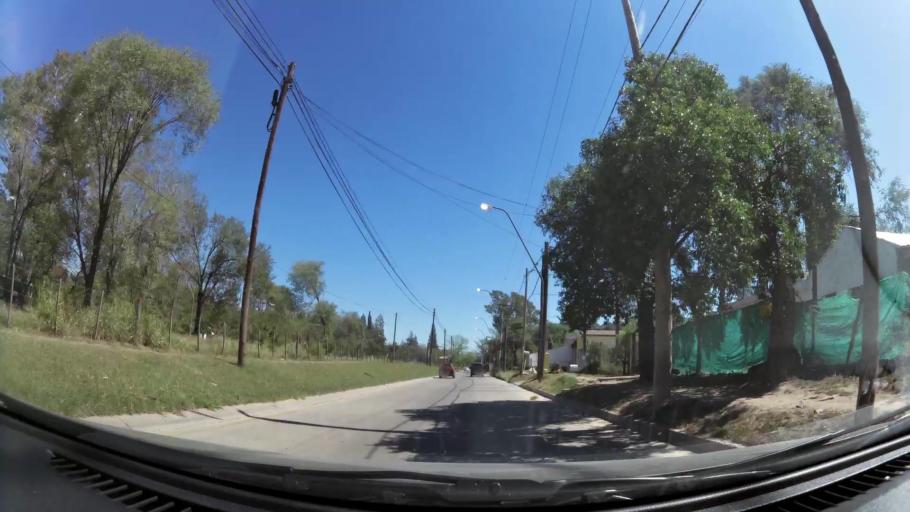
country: AR
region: Cordoba
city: Saldan
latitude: -31.3371
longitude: -64.2826
